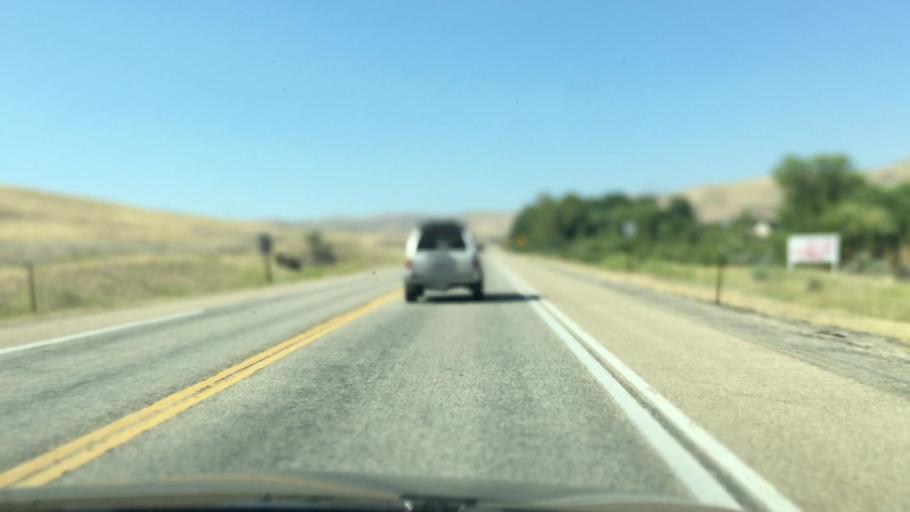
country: US
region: Idaho
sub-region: Ada County
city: Eagle
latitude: 43.7694
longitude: -116.2661
